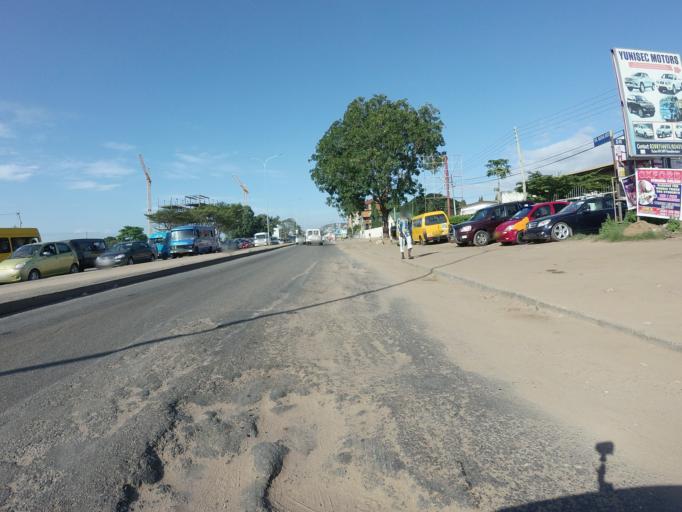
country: GH
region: Greater Accra
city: Gbawe
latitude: 5.5774
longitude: -0.2726
